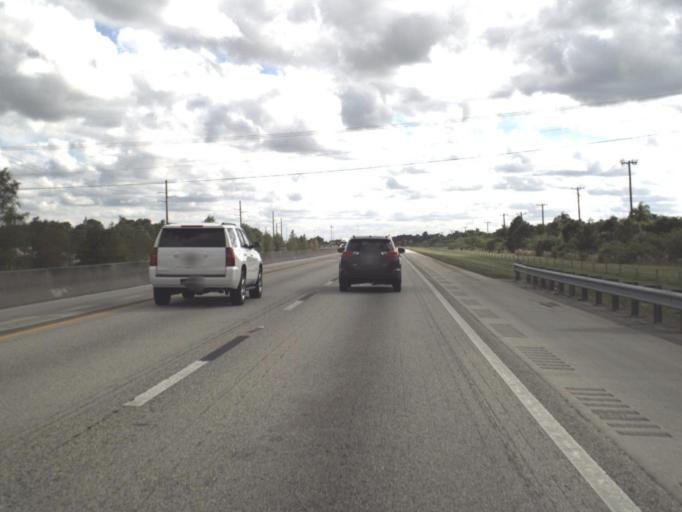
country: US
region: Florida
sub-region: Saint Lucie County
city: River Park
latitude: 27.3175
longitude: -80.3744
